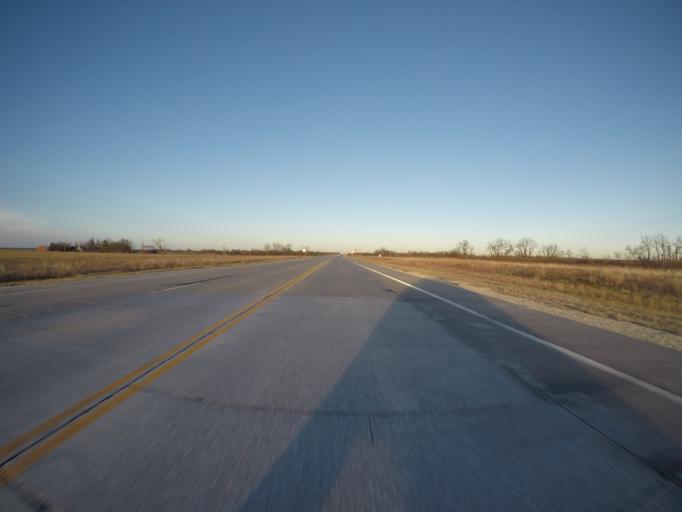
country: US
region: Kansas
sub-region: Harvey County
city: North Newton
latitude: 38.1004
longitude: -97.2762
